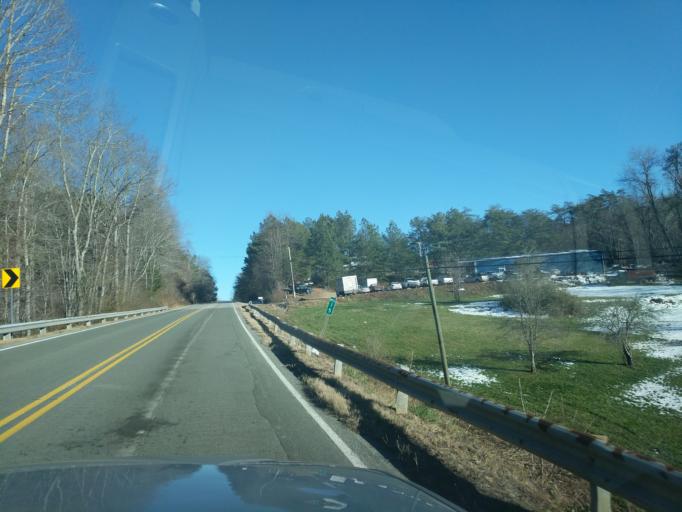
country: US
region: Georgia
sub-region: Towns County
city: Hiawassee
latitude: 34.9250
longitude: -83.6898
